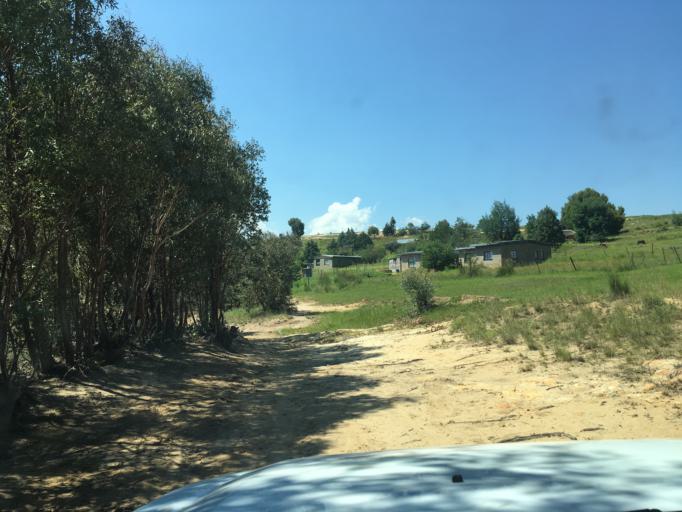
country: LS
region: Butha-Buthe
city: Butha-Buthe
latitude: -28.7250
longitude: 28.3618
